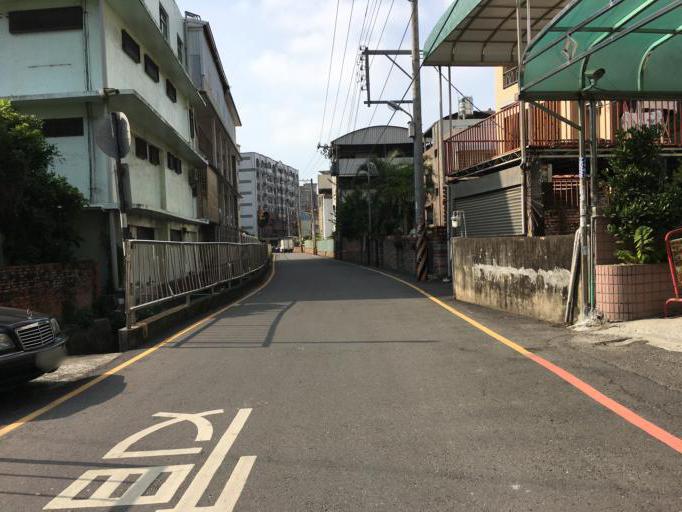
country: TW
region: Taiwan
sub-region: Changhua
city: Chang-hua
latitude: 24.0813
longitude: 120.5539
